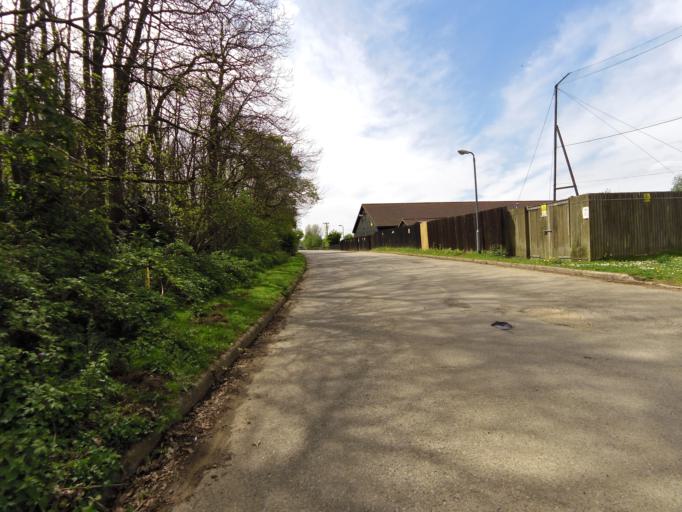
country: GB
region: England
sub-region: Suffolk
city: Ipswich
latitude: 52.0272
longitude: 1.1433
